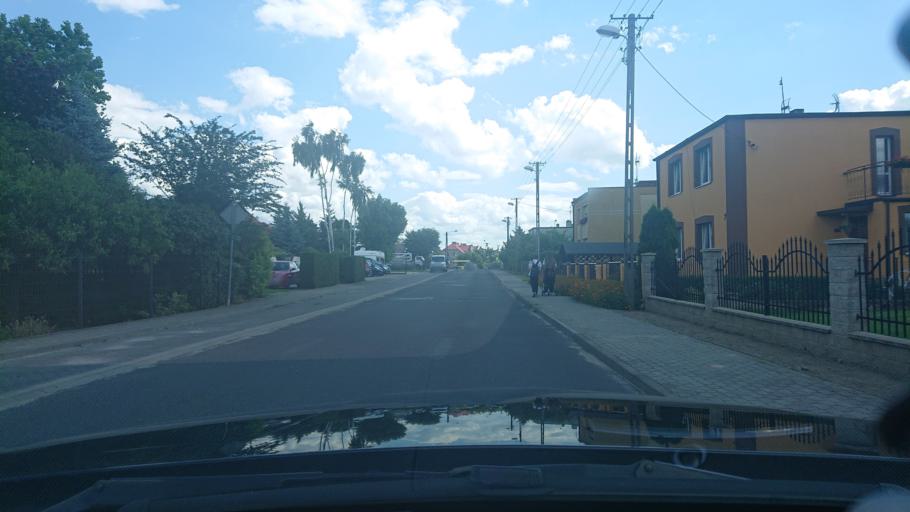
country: PL
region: Greater Poland Voivodeship
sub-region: Powiat gnieznienski
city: Gniezno
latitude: 52.5349
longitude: 17.6353
